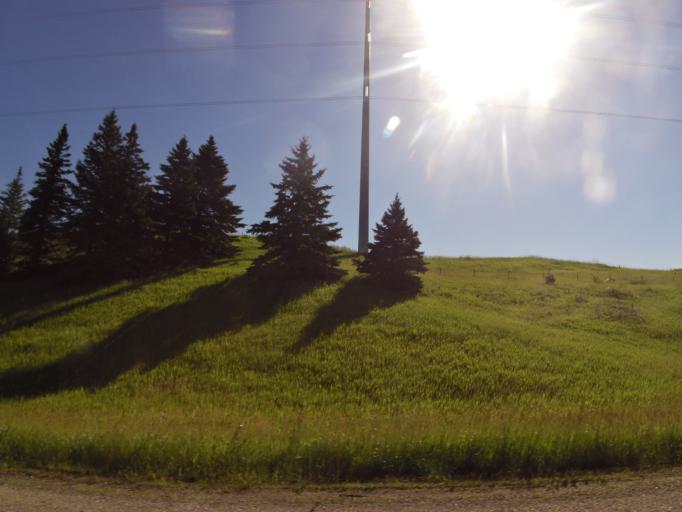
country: US
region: Minnesota
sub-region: Grant County
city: Elbow Lake
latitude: 46.1368
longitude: -95.9246
